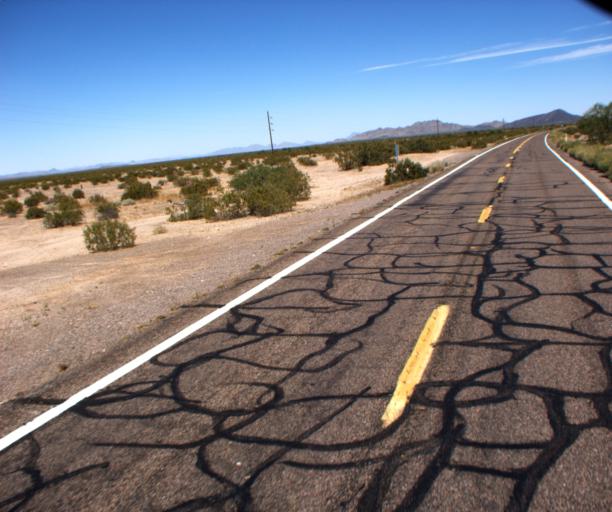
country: US
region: Arizona
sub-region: Maricopa County
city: Gila Bend
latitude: 32.6850
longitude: -112.8551
